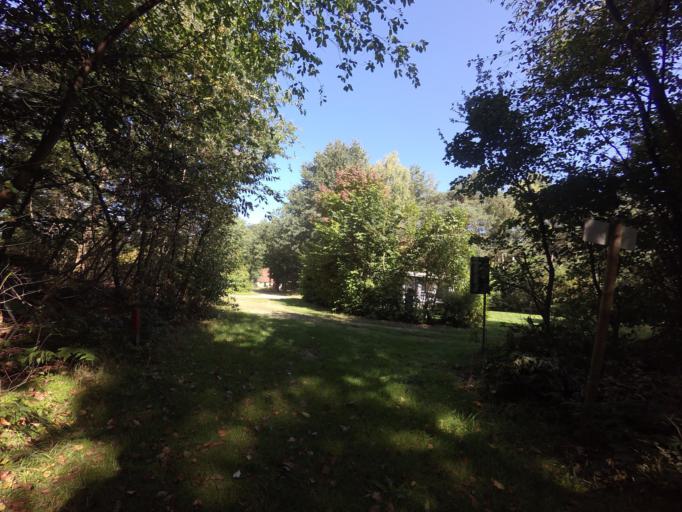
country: DE
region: Lower Saxony
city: Wielen
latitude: 52.5380
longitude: 6.6992
